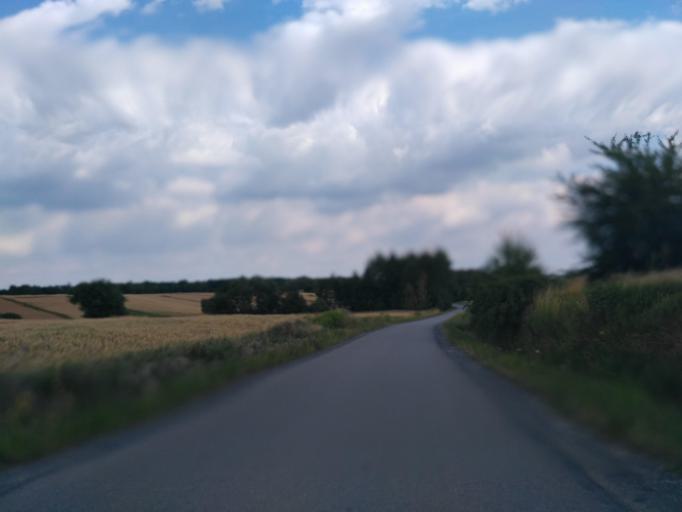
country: PL
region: Subcarpathian Voivodeship
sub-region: Powiat debicki
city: Slotowa
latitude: 49.9535
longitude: 21.2926
